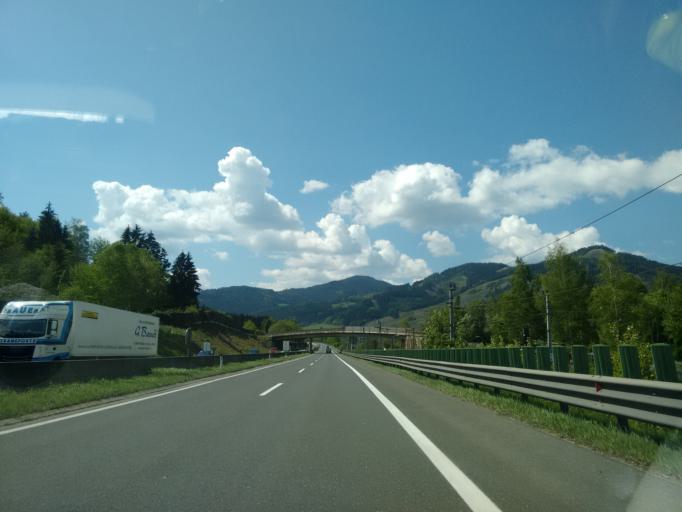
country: AT
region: Styria
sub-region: Politischer Bezirk Bruck-Muerzzuschlag
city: Oberaich
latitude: 47.4044
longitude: 15.2186
